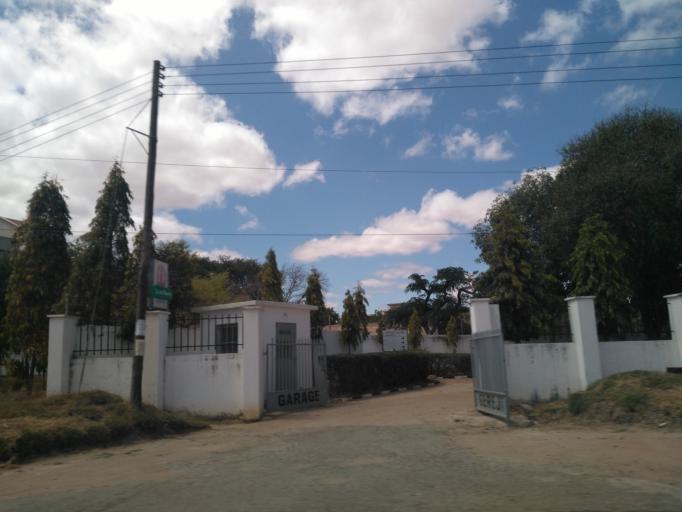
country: TZ
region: Dodoma
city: Dodoma
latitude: -6.1836
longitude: 35.7443
